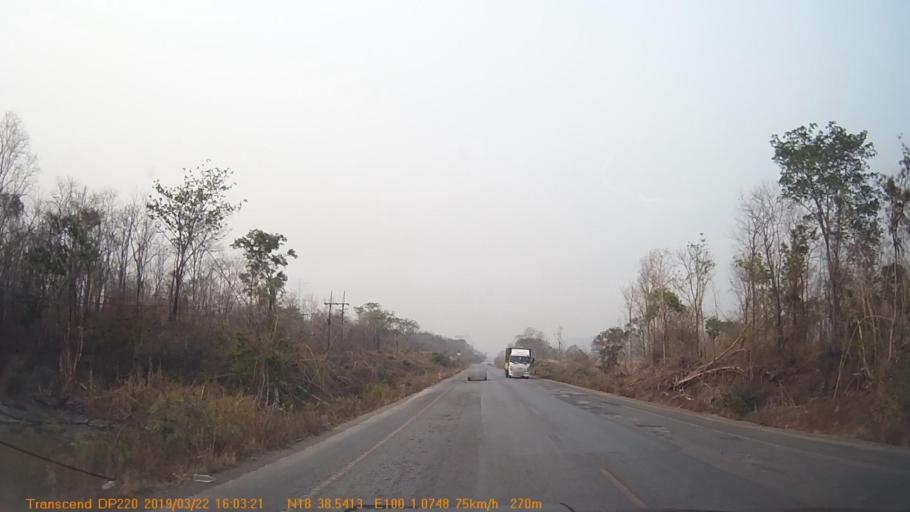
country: TH
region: Lampang
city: Ngao
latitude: 18.6427
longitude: 100.0179
